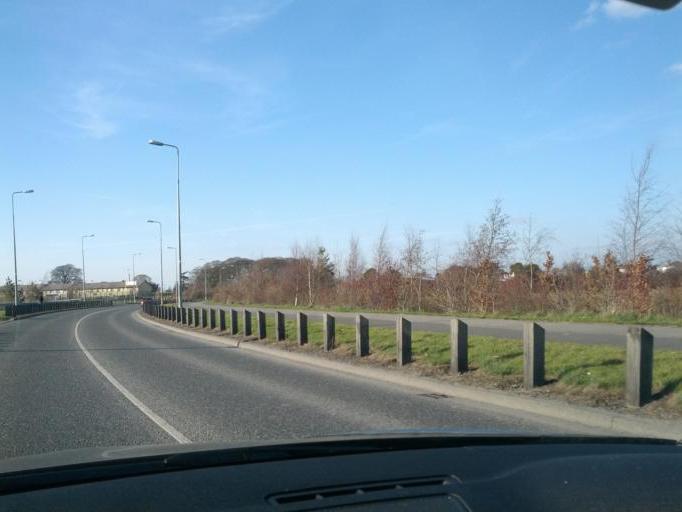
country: IE
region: Leinster
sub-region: Kildare
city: Naas
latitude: 53.2100
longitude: -6.6795
